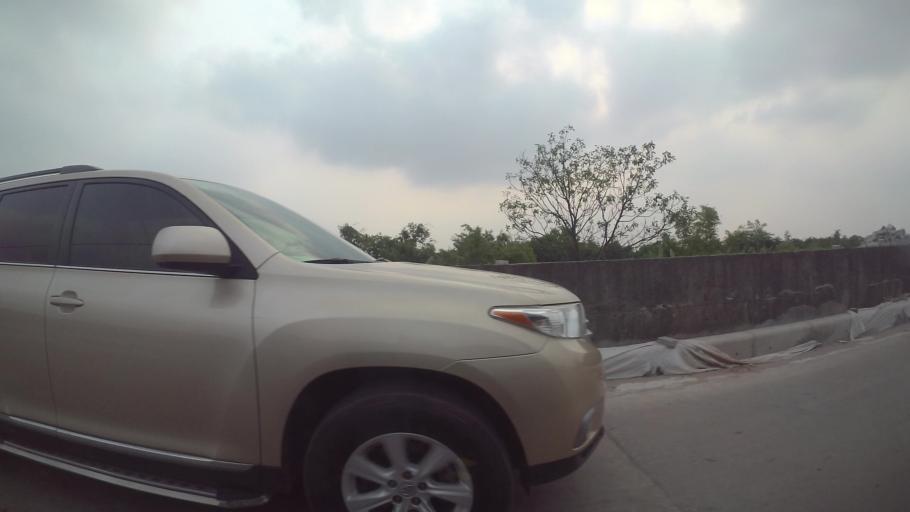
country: VN
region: Ha Noi
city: Trau Quy
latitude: 21.0182
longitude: 105.9042
